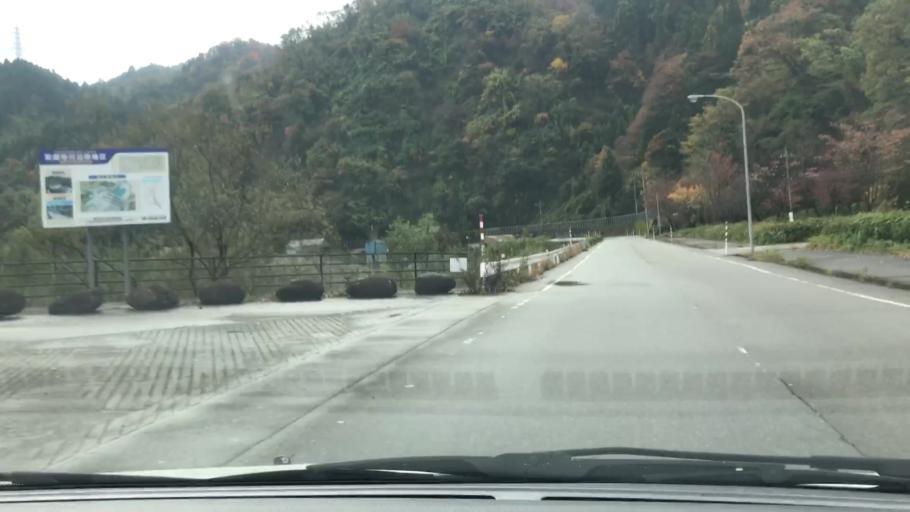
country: JP
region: Toyama
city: Kamiichi
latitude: 36.5801
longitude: 137.3317
